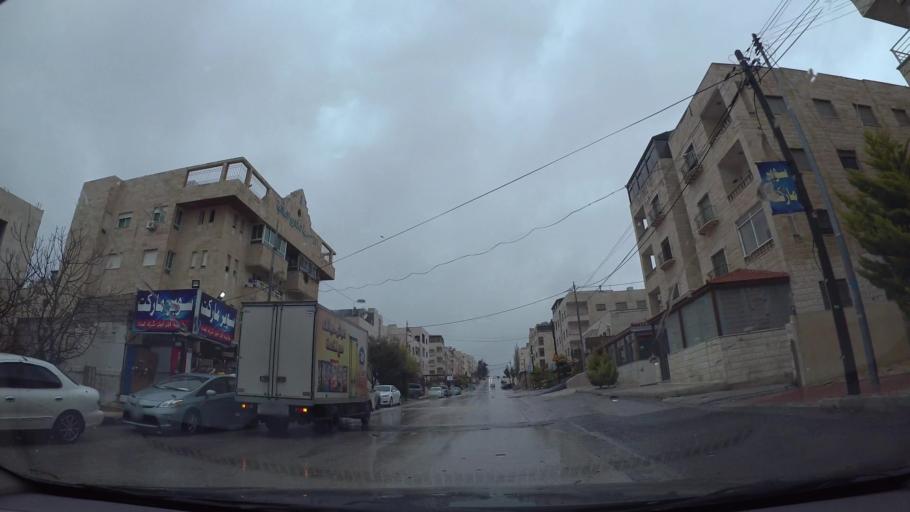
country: JO
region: Amman
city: Al Jubayhah
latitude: 32.0229
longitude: 35.8818
